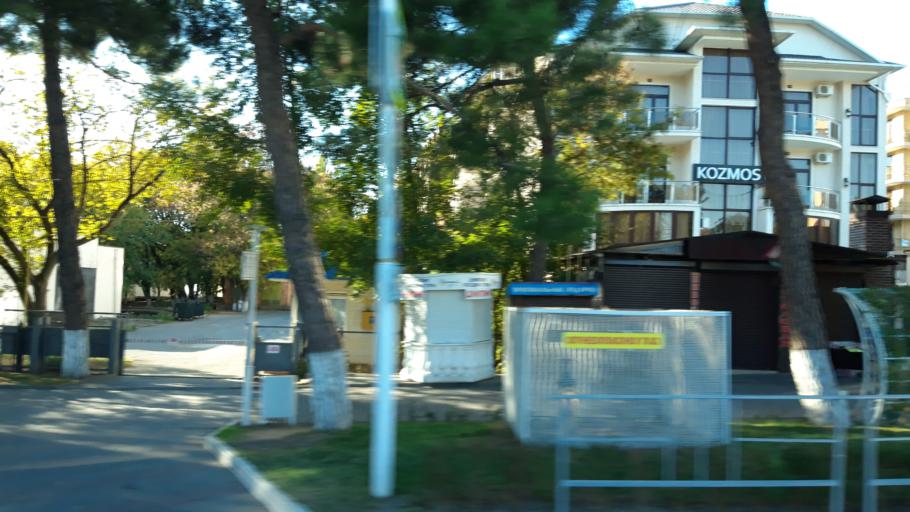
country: RU
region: Krasnodarskiy
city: Kabardinka
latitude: 44.6490
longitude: 37.9371
